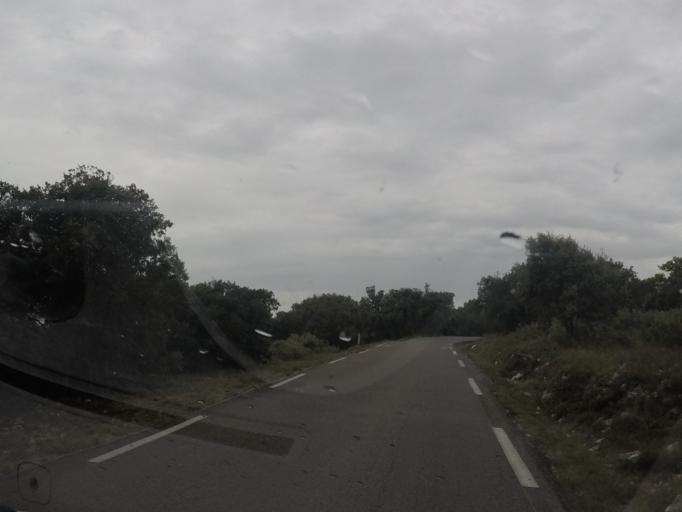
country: FR
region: Provence-Alpes-Cote d'Azur
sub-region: Departement du Vaucluse
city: Gordes
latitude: 43.9229
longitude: 5.1895
